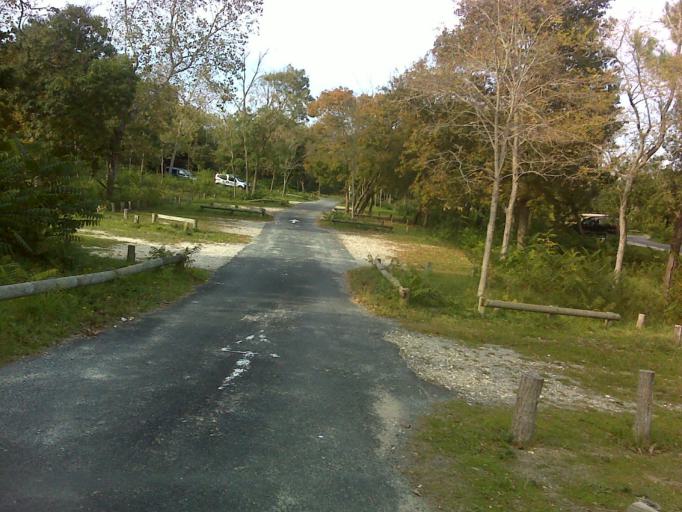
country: FR
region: Poitou-Charentes
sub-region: Departement de la Charente-Maritime
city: Les Mathes
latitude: 45.7285
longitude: -1.2291
